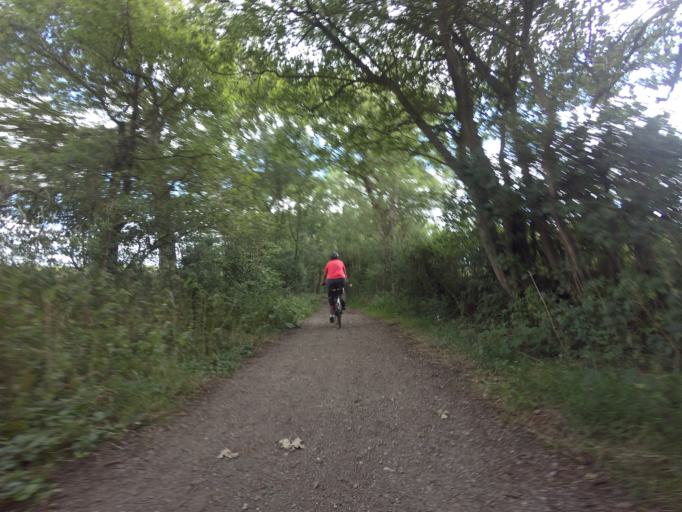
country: GB
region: England
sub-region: East Sussex
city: Hailsham
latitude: 50.8377
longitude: 0.2226
